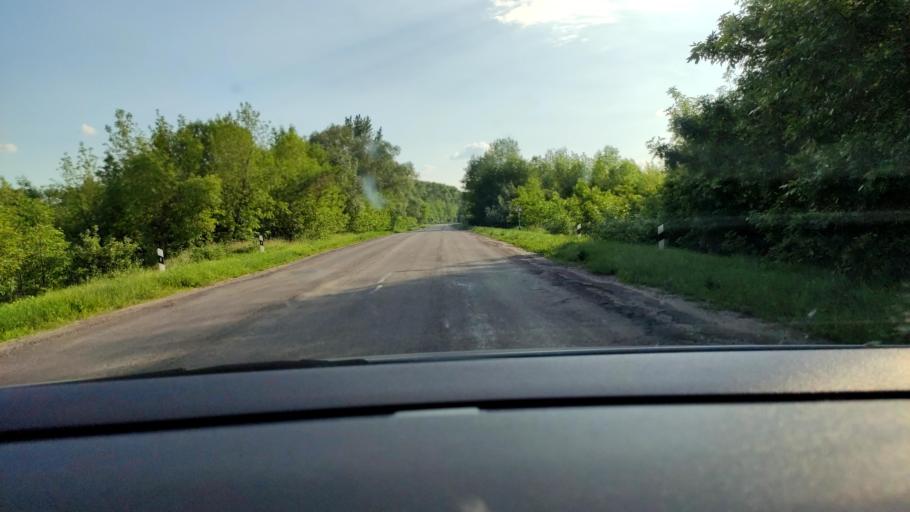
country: RU
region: Voronezj
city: Panino
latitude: 51.5841
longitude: 39.9532
